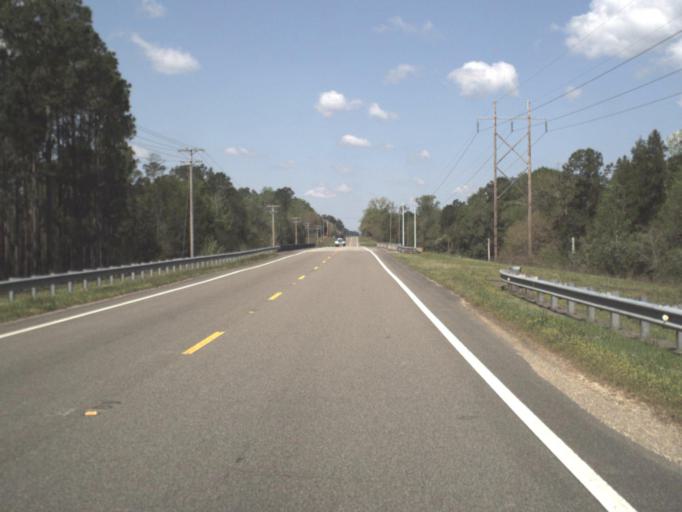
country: US
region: Florida
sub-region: Santa Rosa County
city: Point Baker
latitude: 30.8626
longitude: -86.9027
